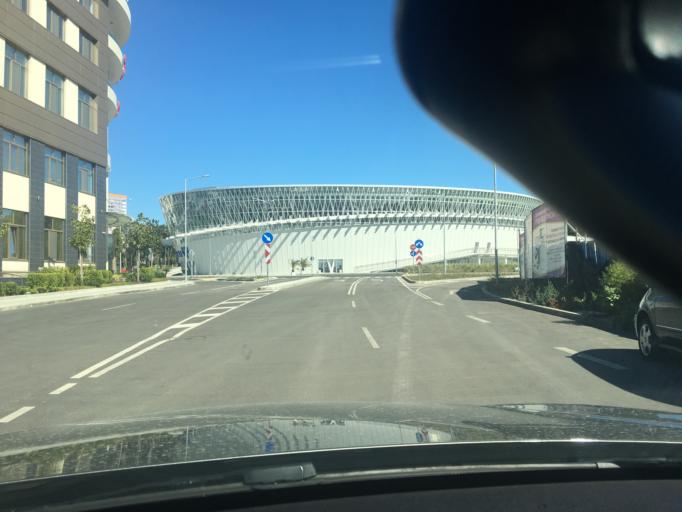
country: BG
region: Burgas
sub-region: Obshtina Burgas
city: Burgas
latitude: 42.5115
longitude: 27.4579
